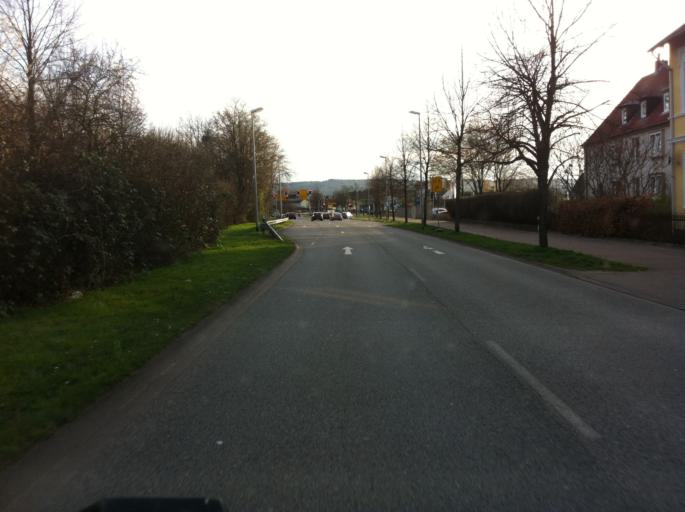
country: DE
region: North Rhine-Westphalia
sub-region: Regierungsbezirk Detmold
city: Minden
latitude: 52.2794
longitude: 8.9058
